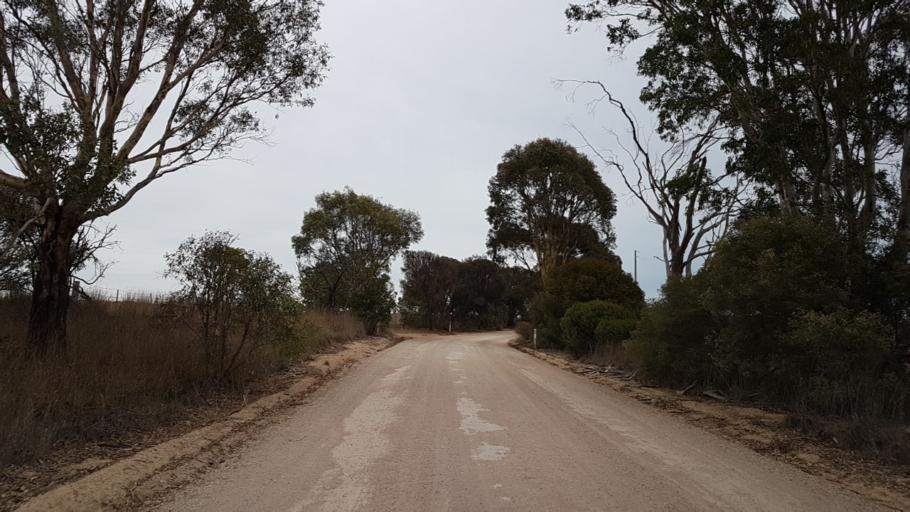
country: AU
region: South Australia
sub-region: Mount Barker
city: Nairne
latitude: -34.9991
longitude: 138.9785
